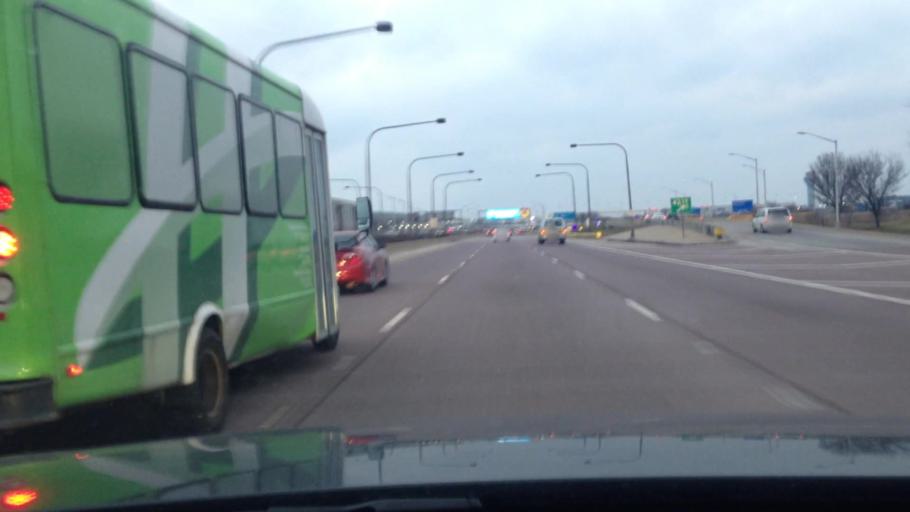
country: US
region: Illinois
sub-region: Cook County
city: Rosemont
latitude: 41.9790
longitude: -87.8839
